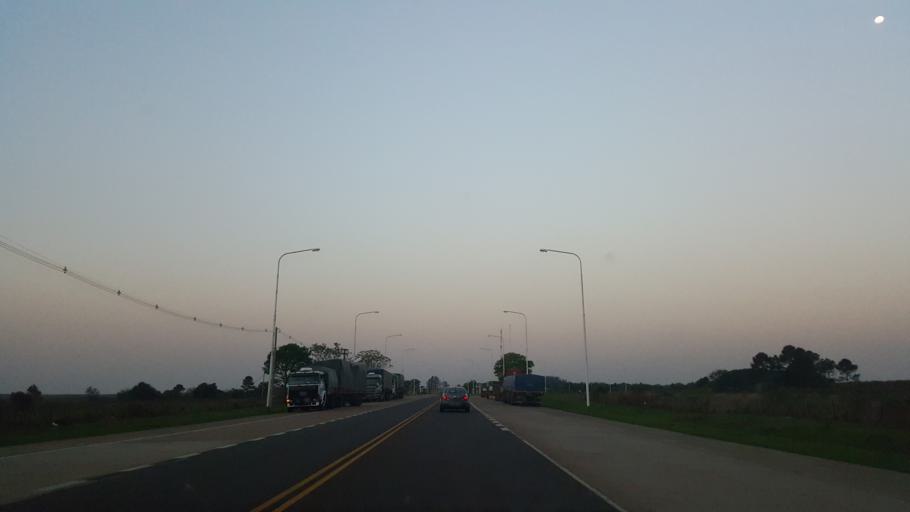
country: PY
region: Itapua
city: San Juan del Parana
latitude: -27.4532
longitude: -56.0473
